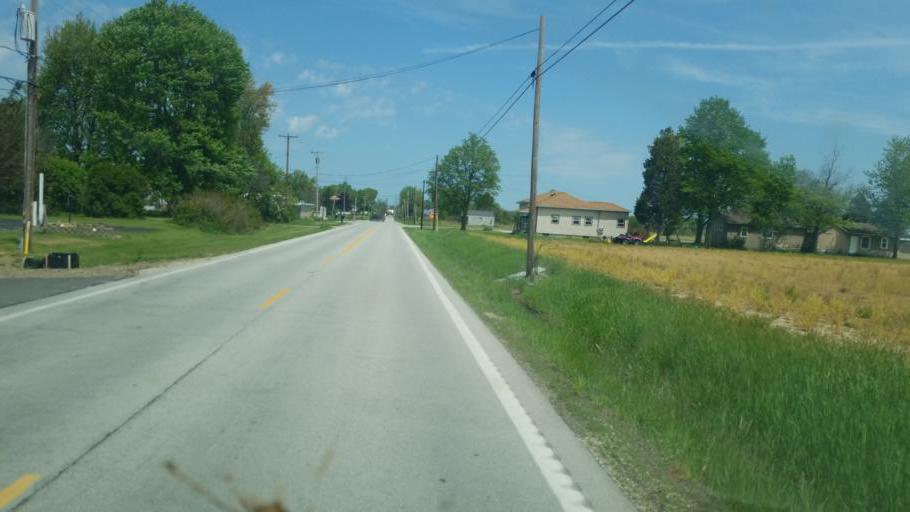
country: US
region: Ohio
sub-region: Ottawa County
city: Oak Harbor
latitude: 41.4960
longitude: -83.1452
